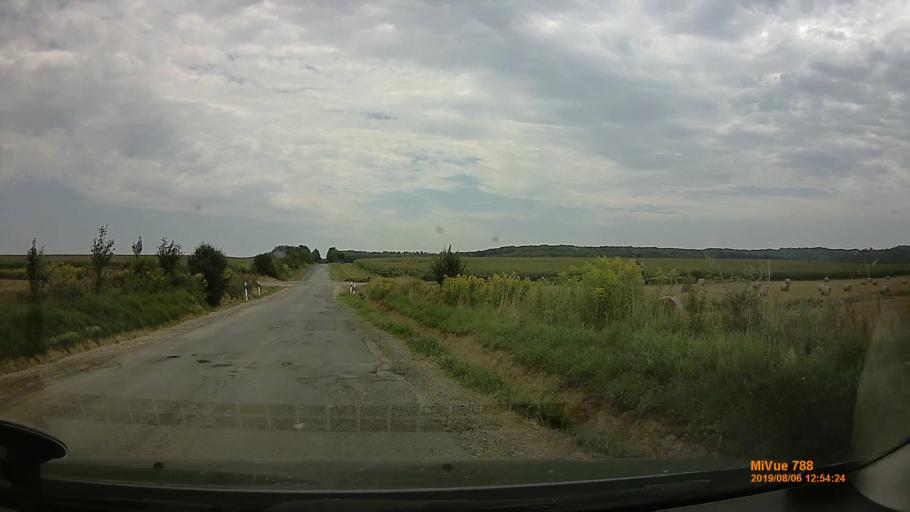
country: HU
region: Zala
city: Pacsa
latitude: 46.6373
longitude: 17.0125
